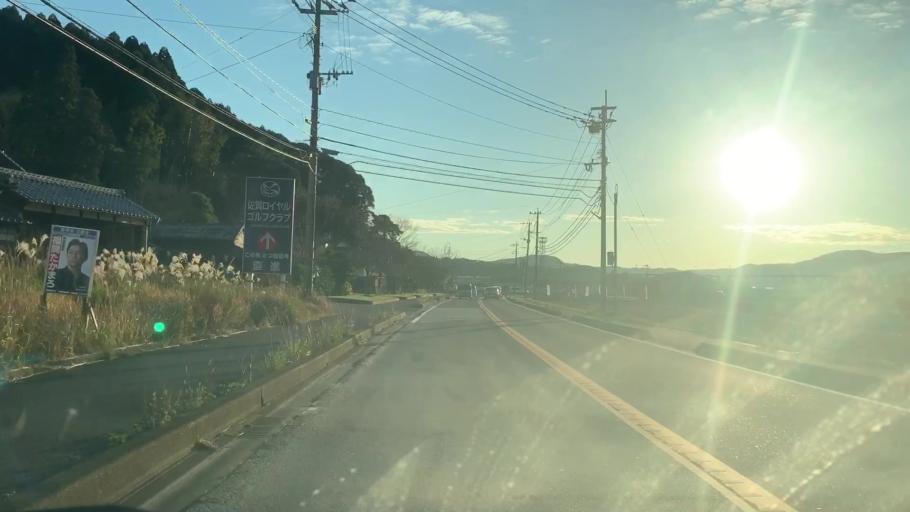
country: JP
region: Saga Prefecture
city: Karatsu
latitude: 33.3576
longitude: 130.0066
